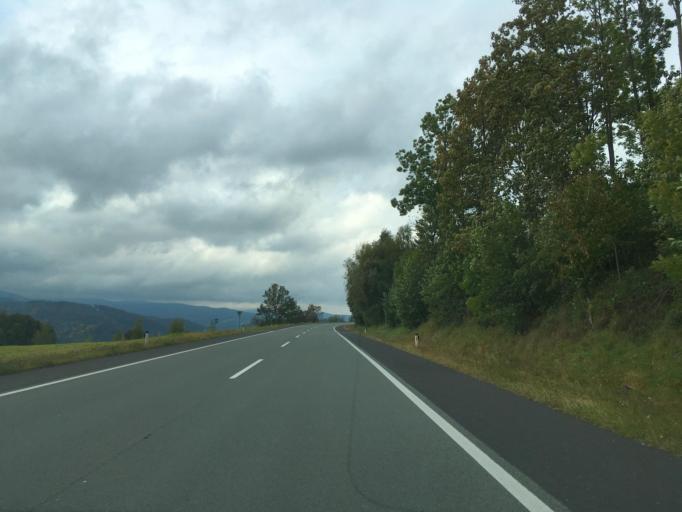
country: AT
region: Styria
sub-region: Politischer Bezirk Hartberg-Fuerstenfeld
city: Pinggau
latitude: 47.4411
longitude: 16.0779
